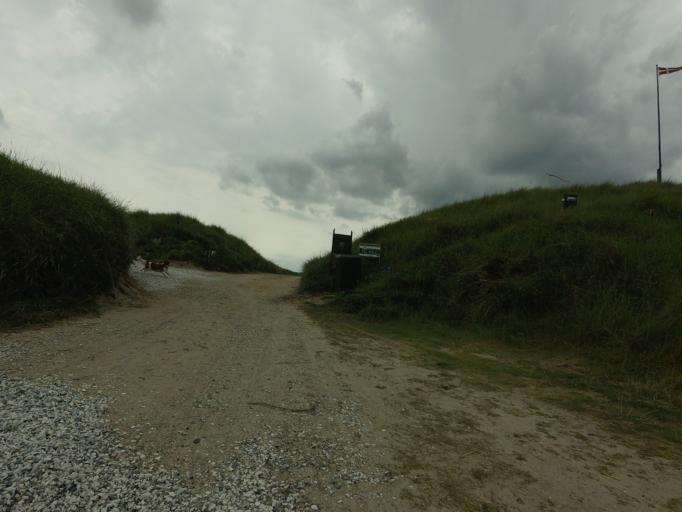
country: DK
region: North Denmark
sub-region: Jammerbugt Kommune
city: Pandrup
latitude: 57.3103
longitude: 9.6484
